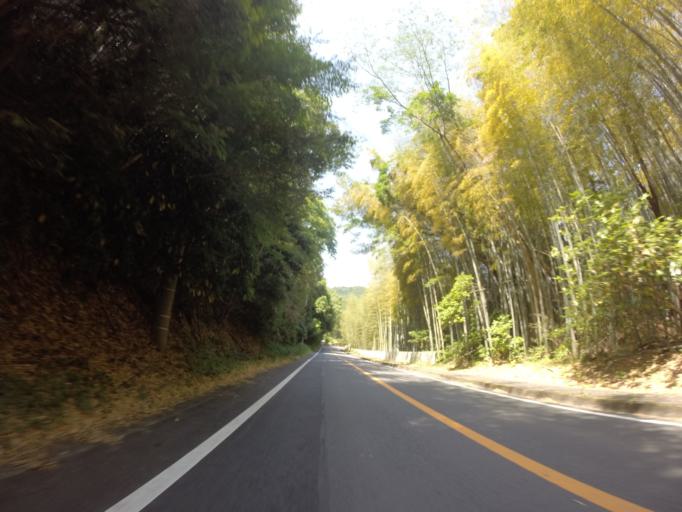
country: JP
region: Shizuoka
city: Fujinomiya
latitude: 35.1965
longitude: 138.5735
